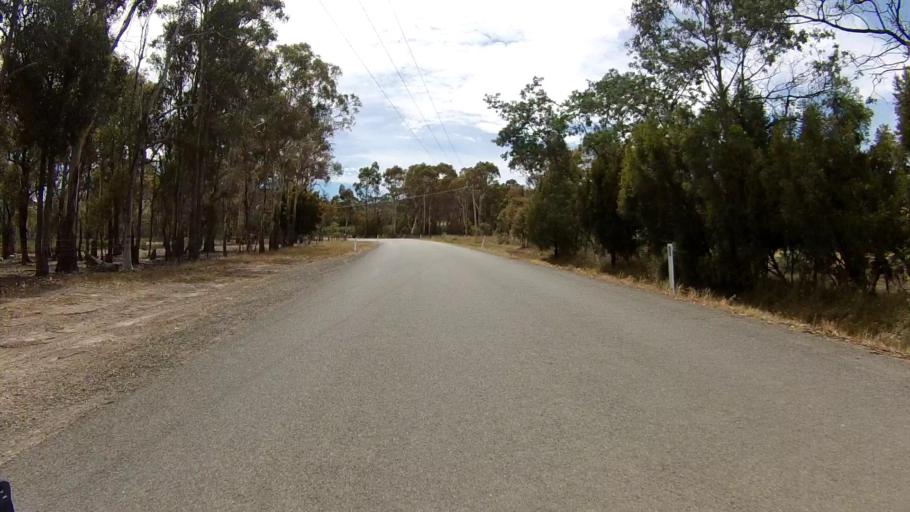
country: AU
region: Tasmania
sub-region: Sorell
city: Sorell
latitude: -42.8040
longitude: 147.6433
